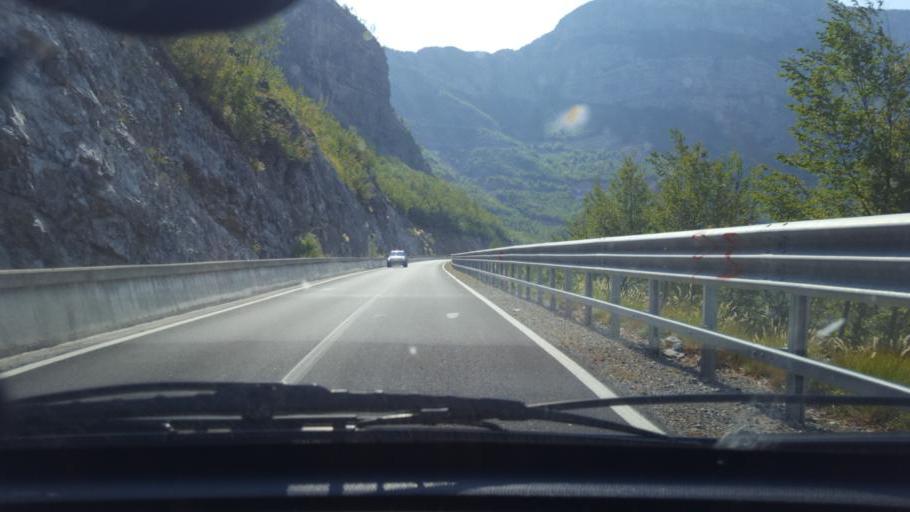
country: AL
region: Shkoder
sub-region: Rrethi i Malesia e Madhe
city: Kastrat
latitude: 42.4200
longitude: 19.5030
